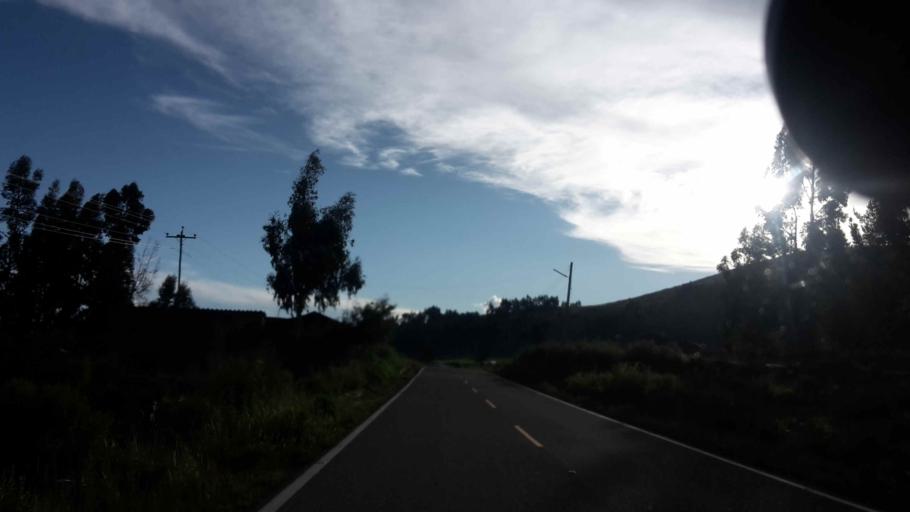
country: BO
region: Cochabamba
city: Arani
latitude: -17.5521
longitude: -65.6907
